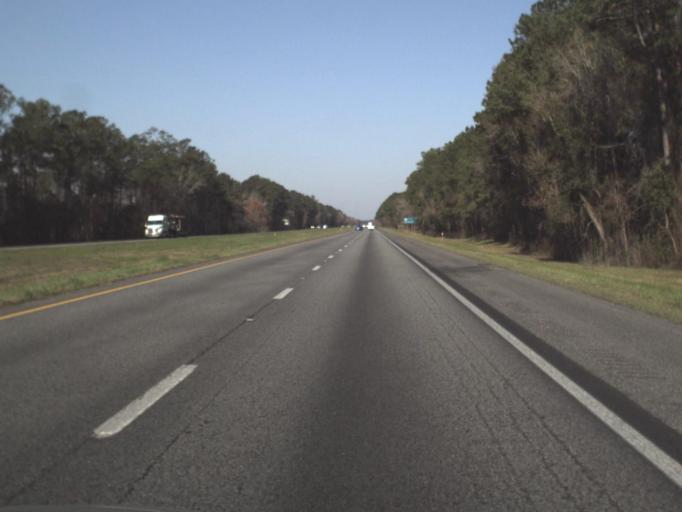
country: US
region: Florida
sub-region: Jefferson County
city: Monticello
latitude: 30.4598
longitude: -83.7772
